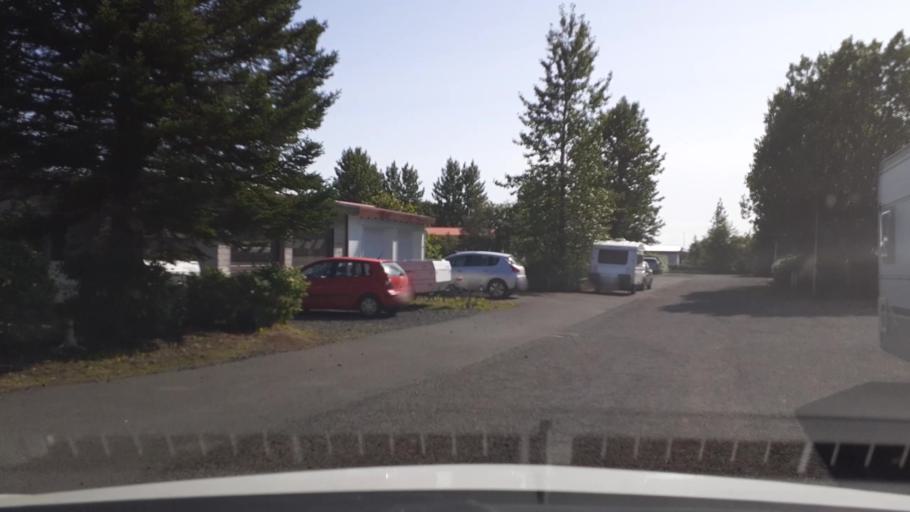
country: IS
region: South
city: Hveragerdi
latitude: 64.0047
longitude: -21.2025
